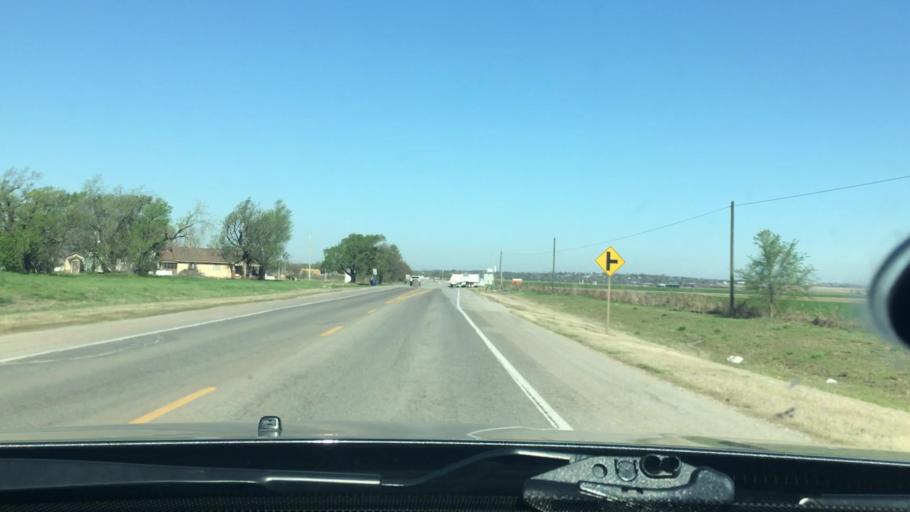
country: US
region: Oklahoma
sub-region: Garvin County
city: Lindsay
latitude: 34.8327
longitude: -97.5785
